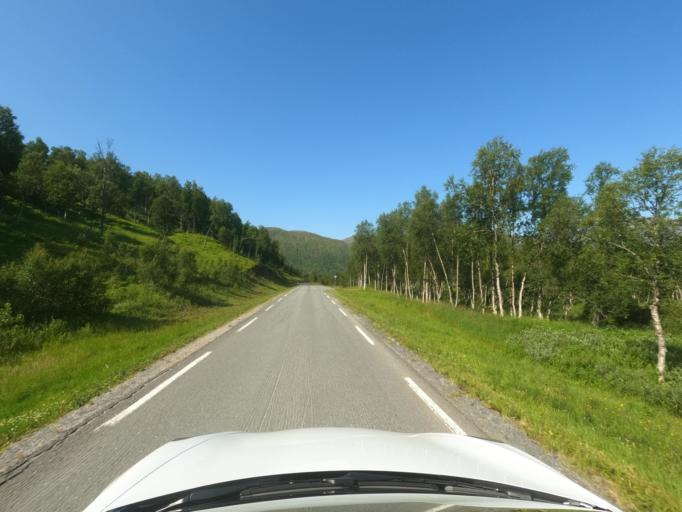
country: NO
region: Troms
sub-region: Skanland
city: Evenskjer
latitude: 68.3284
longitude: 16.5633
